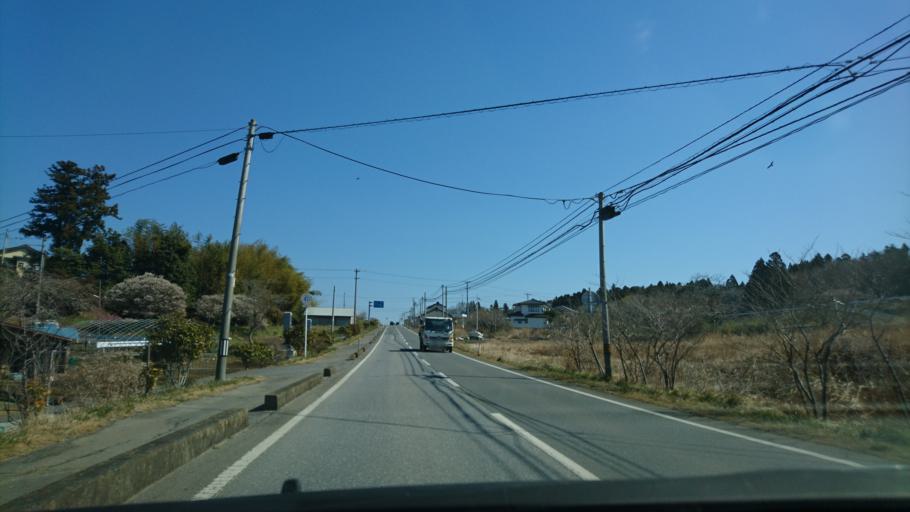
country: JP
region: Iwate
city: Ofunato
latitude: 38.8440
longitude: 141.6174
